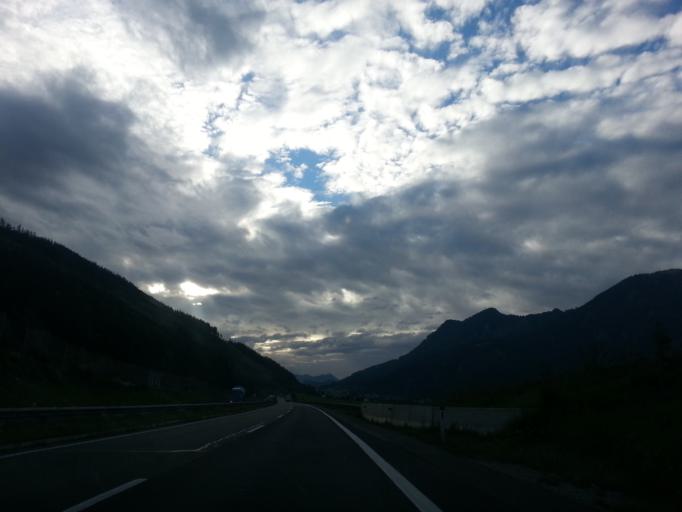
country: AT
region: Styria
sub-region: Politischer Bezirk Leoben
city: Kammern im Liesingtal
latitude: 47.3825
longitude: 14.9376
